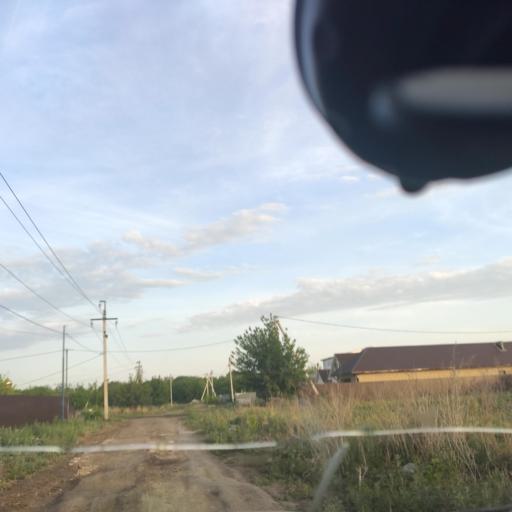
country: RU
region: Samara
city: Tol'yatti
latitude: 53.5730
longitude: 49.4074
